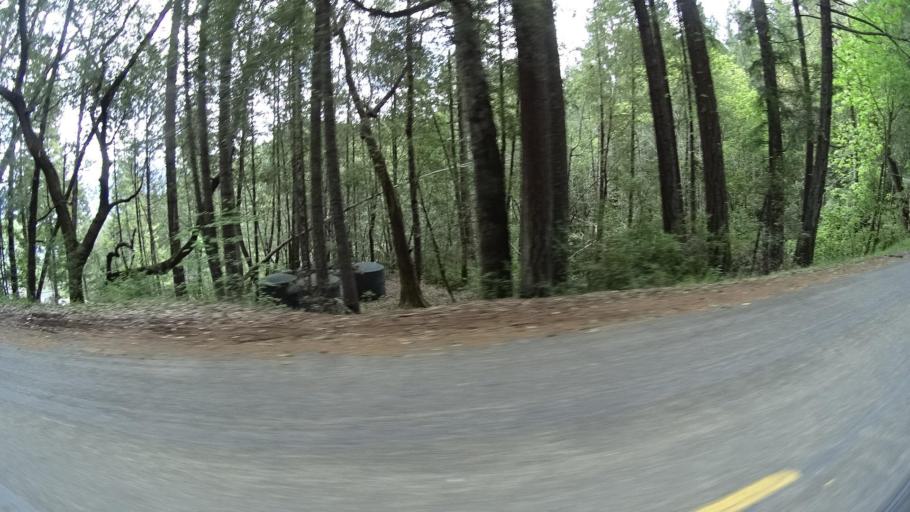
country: US
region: California
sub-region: Humboldt County
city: Redway
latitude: 40.1402
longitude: -123.6302
